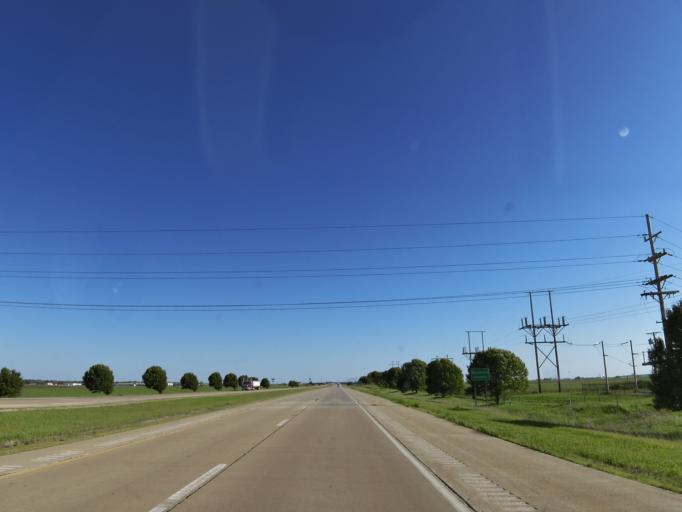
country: US
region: Illinois
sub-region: Woodford County
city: Minonk
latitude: 40.9265
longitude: -89.0568
